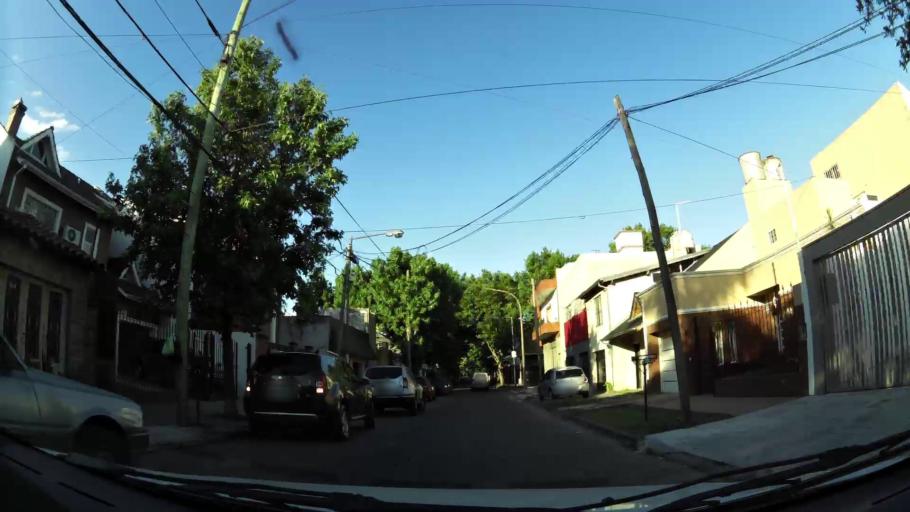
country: AR
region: Buenos Aires
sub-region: Partido de General San Martin
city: General San Martin
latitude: -34.5678
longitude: -58.5444
